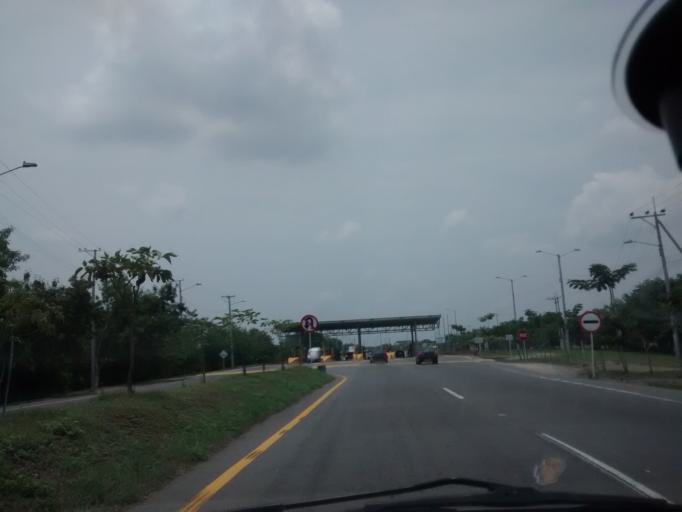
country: CO
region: Tolima
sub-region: Flandes
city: Flandes
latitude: 4.2461
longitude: -74.8796
